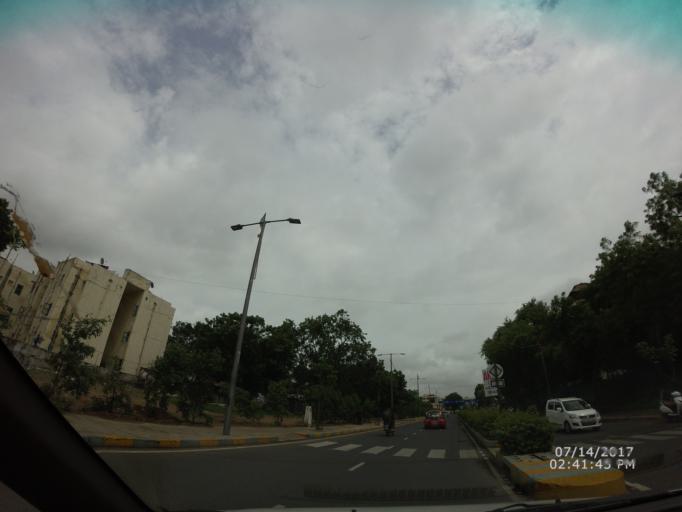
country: IN
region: Gujarat
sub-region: Ahmadabad
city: Ahmedabad
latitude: 23.0645
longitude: 72.5963
